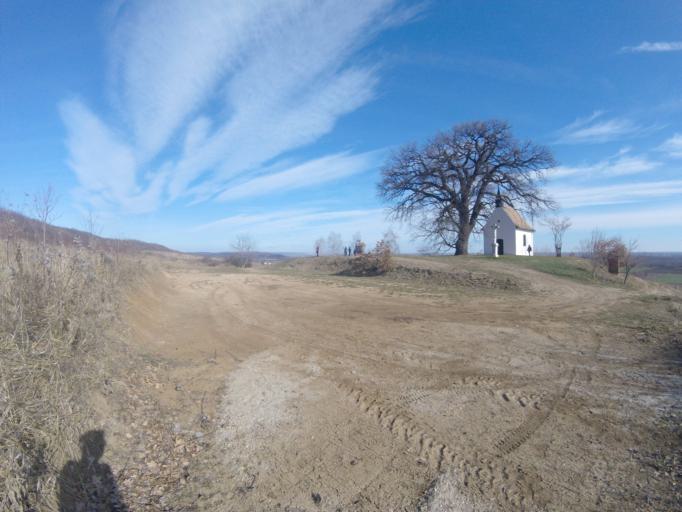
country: HU
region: Tolna
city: Bataszek
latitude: 46.1697
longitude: 18.7001
